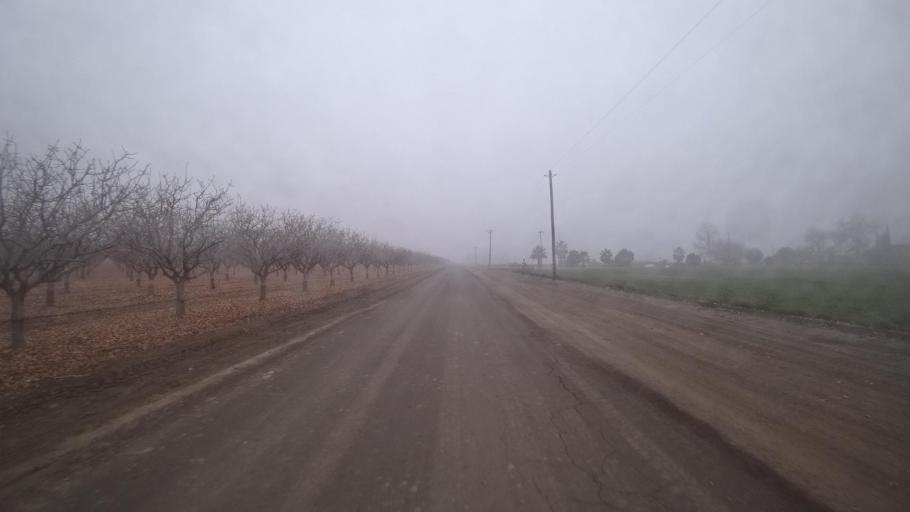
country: US
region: California
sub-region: Kern County
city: Buttonwillow
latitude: 35.4268
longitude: -119.5430
